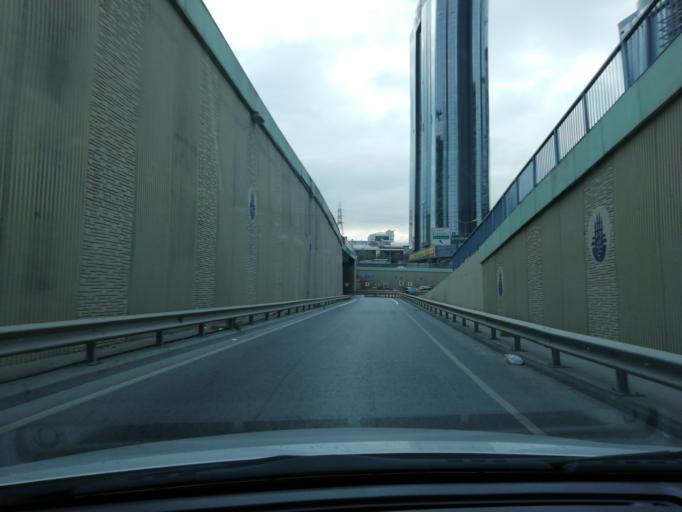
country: TR
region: Istanbul
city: Mahmutbey
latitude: 41.0455
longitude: 28.8097
